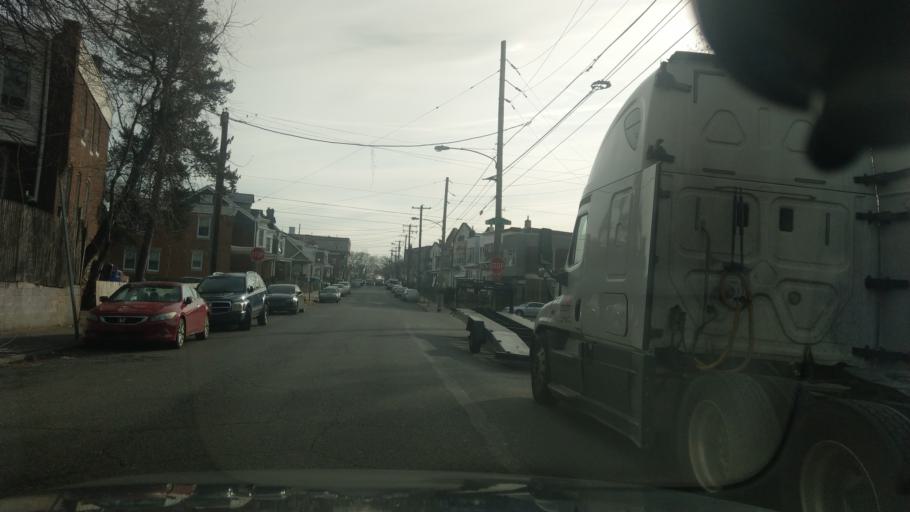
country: US
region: Pennsylvania
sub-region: Montgomery County
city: Jenkintown
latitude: 40.0356
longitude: -75.1333
